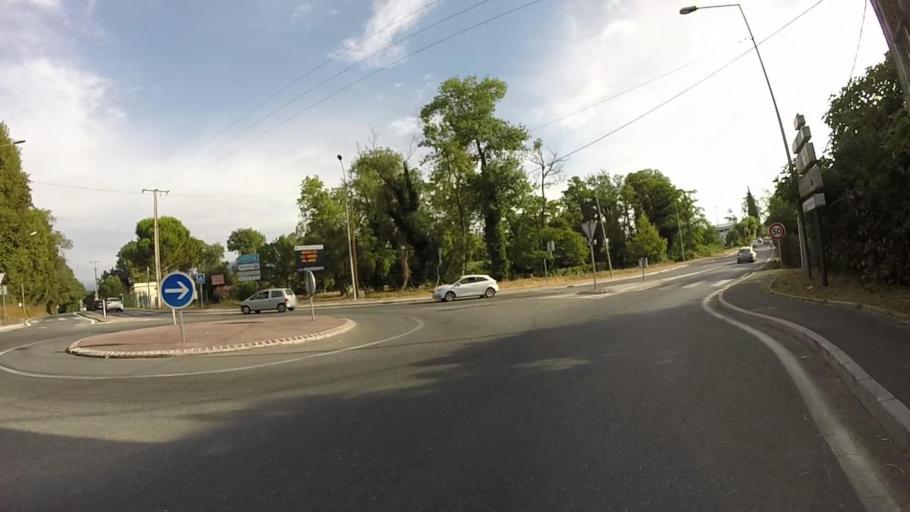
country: FR
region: Provence-Alpes-Cote d'Azur
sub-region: Departement des Alpes-Maritimes
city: Biot
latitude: 43.6149
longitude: 7.1085
